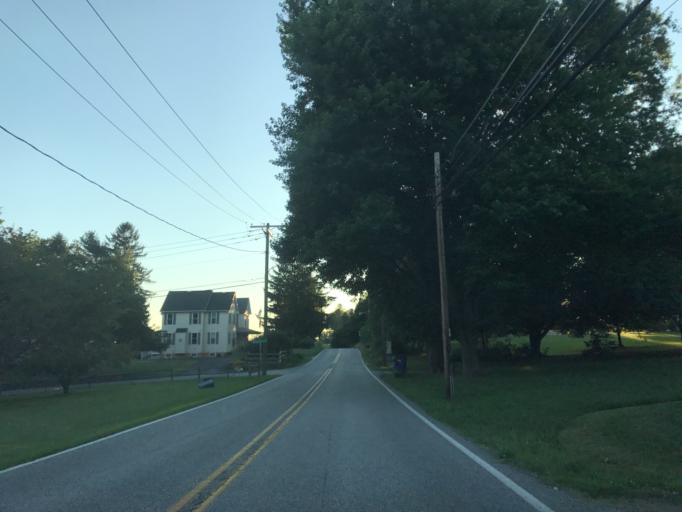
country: US
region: Maryland
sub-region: Harford County
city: Jarrettsville
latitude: 39.6009
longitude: -76.4866
